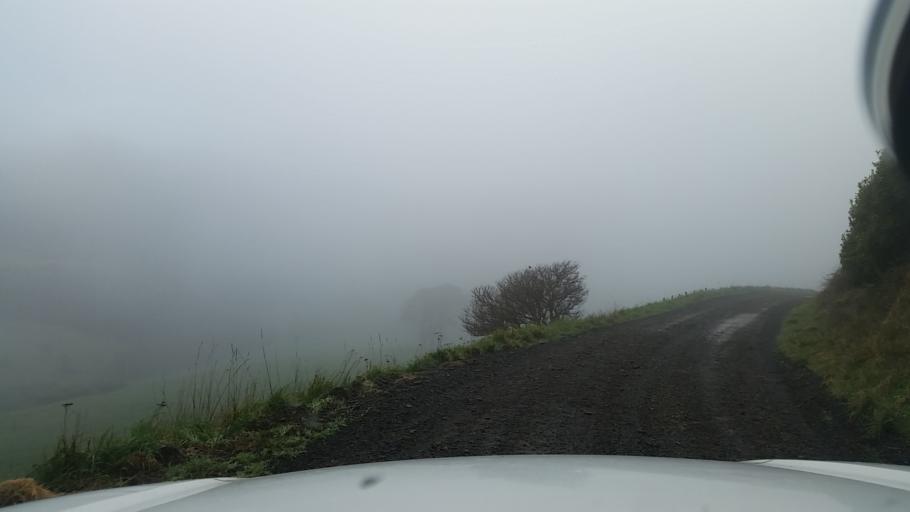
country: NZ
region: Canterbury
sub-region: Christchurch City
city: Christchurch
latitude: -43.7369
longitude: 172.8949
